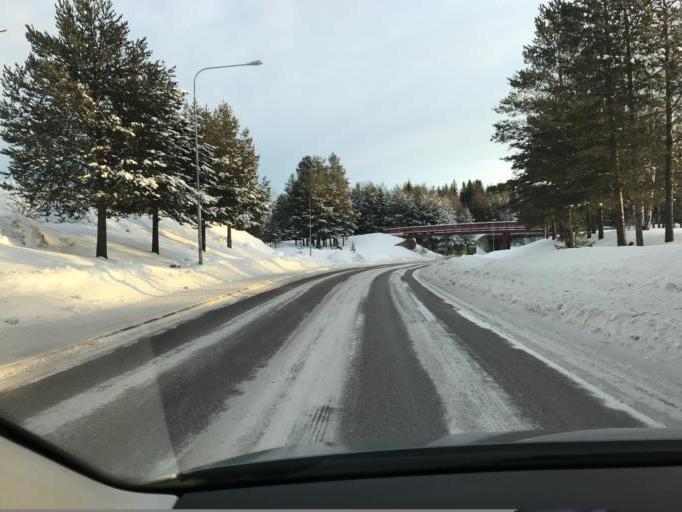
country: SE
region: Norrbotten
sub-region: Lulea Kommun
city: Gammelstad
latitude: 65.6199
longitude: 22.0540
